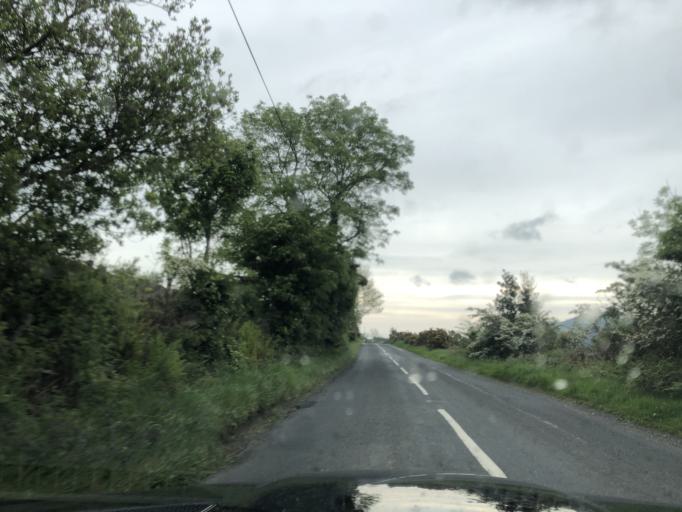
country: GB
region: Northern Ireland
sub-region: Down District
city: Castlewellan
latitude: 54.2226
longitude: -5.9773
